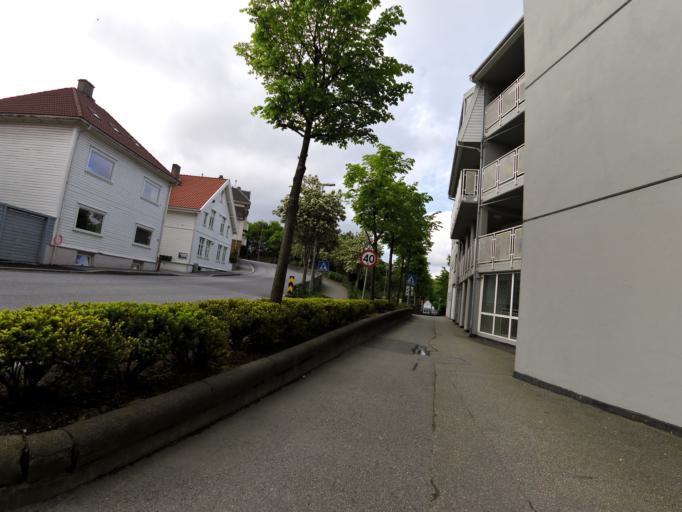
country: NO
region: Rogaland
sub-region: Stavanger
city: Stavanger
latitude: 58.9670
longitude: 5.7355
